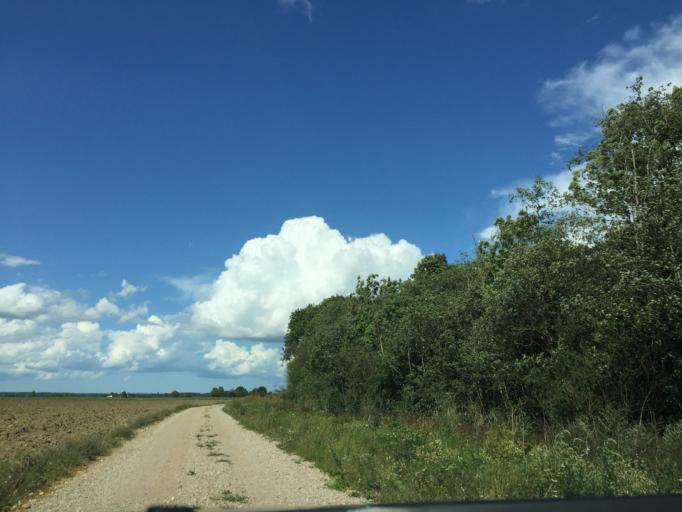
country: LT
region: Siauliu apskritis
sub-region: Joniskis
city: Joniskis
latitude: 56.3564
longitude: 23.5804
